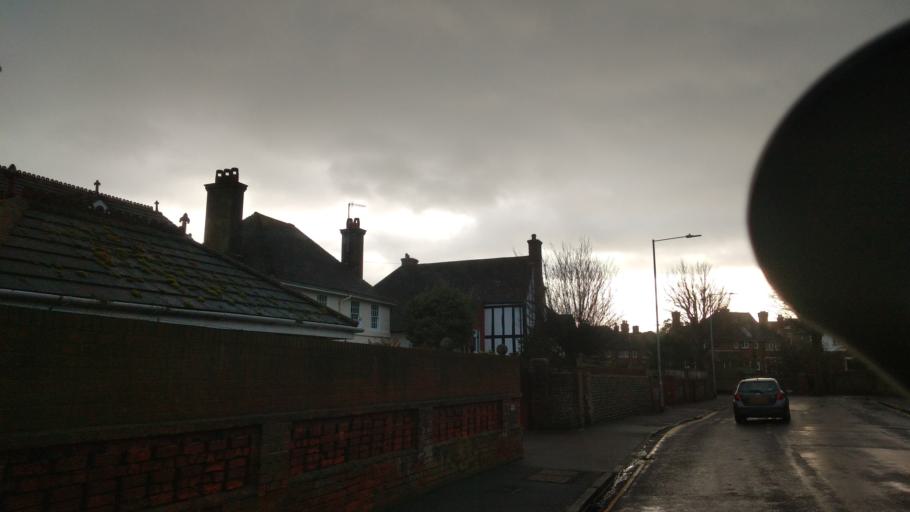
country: GB
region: England
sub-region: East Sussex
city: Eastbourne
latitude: 50.7714
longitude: 0.2742
